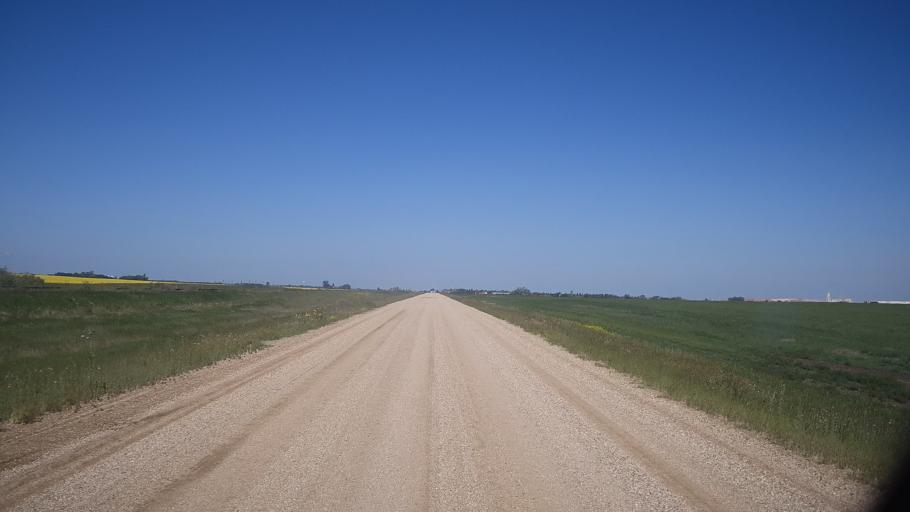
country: CA
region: Saskatchewan
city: Watrous
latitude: 51.8793
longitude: -106.0176
